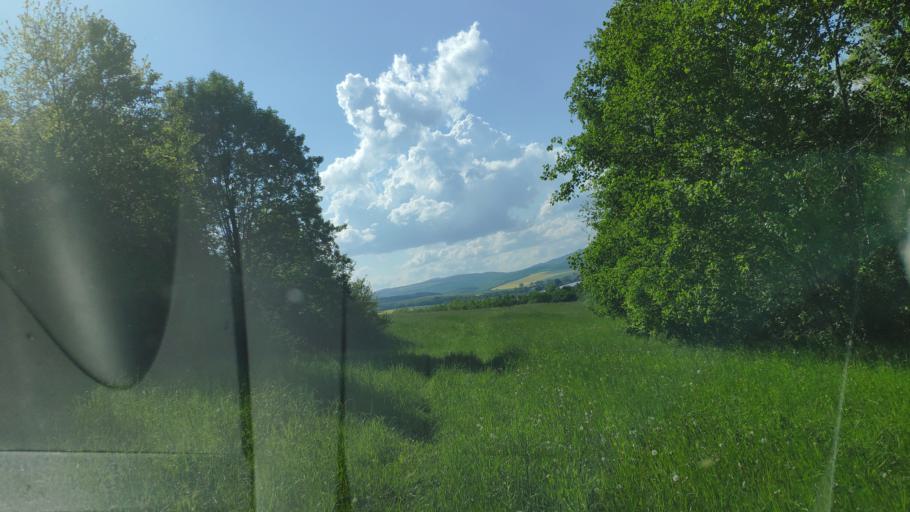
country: SK
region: Presovsky
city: Sabinov
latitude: 49.0527
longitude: 21.1496
